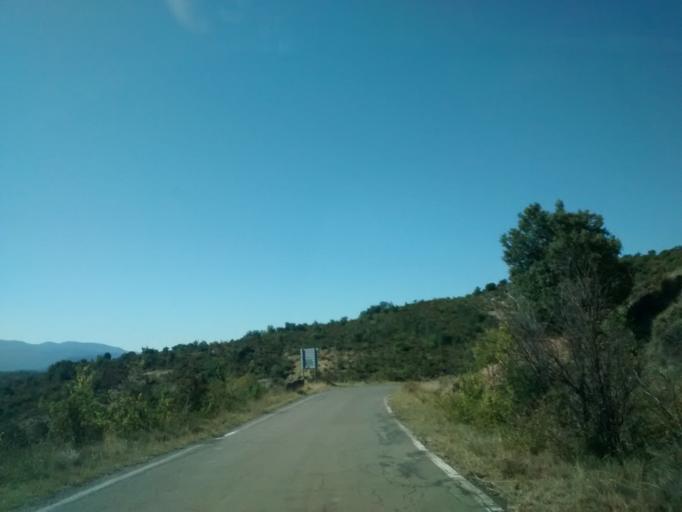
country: ES
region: Aragon
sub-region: Provincia de Huesca
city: Santa Cruz de la Seros
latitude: 42.4758
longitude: -0.5948
